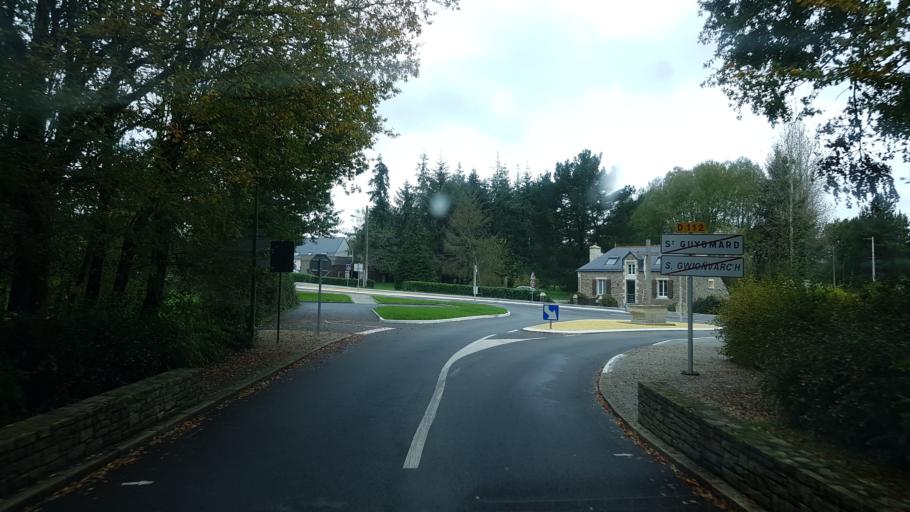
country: FR
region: Brittany
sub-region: Departement du Morbihan
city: Serent
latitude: 47.7824
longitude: -2.5158
